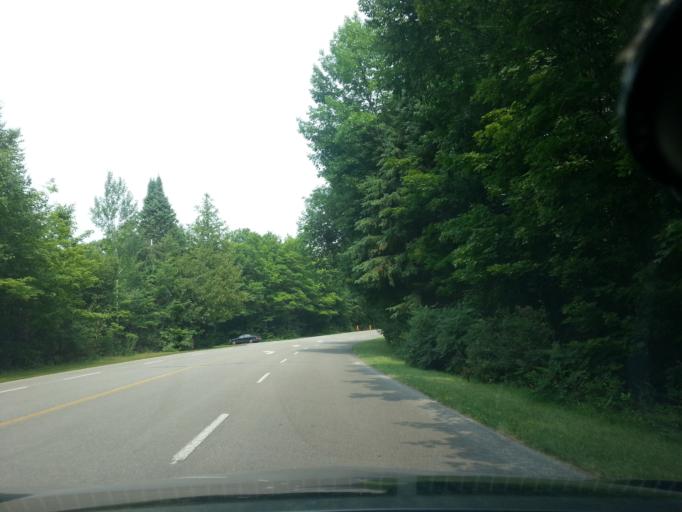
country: CA
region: Quebec
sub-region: Outaouais
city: Gatineau
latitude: 45.4709
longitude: -75.8280
